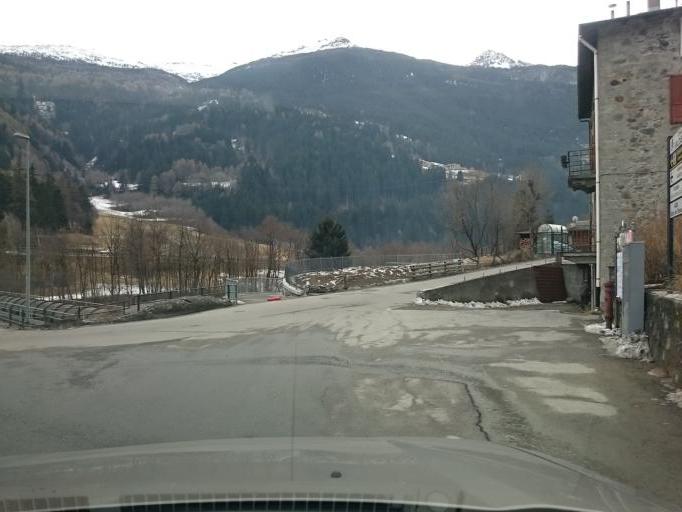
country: IT
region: Lombardy
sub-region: Provincia di Sondrio
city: Cepina
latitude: 46.4391
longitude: 10.3562
